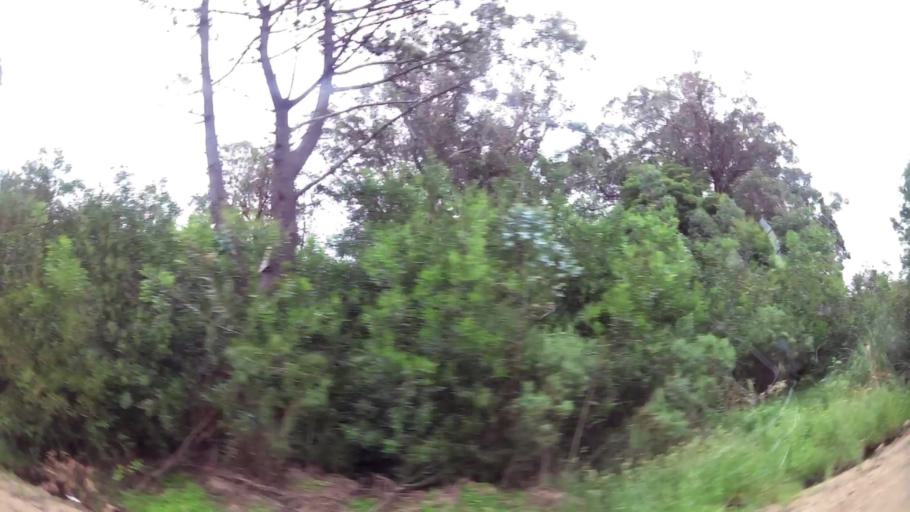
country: UY
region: Maldonado
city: Maldonado
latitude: -34.9029
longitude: -55.0382
